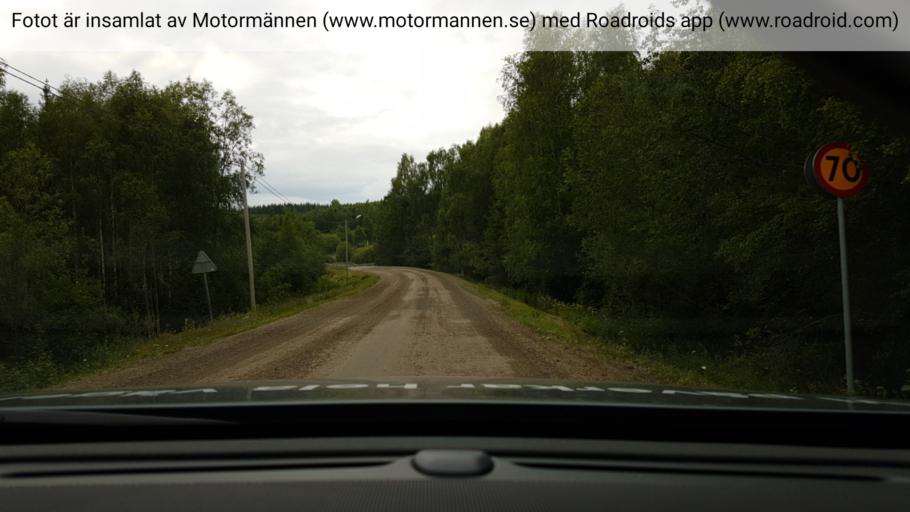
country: SE
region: Vaesterbotten
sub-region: Vannas Kommun
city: Vannasby
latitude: 64.0997
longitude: 20.0026
